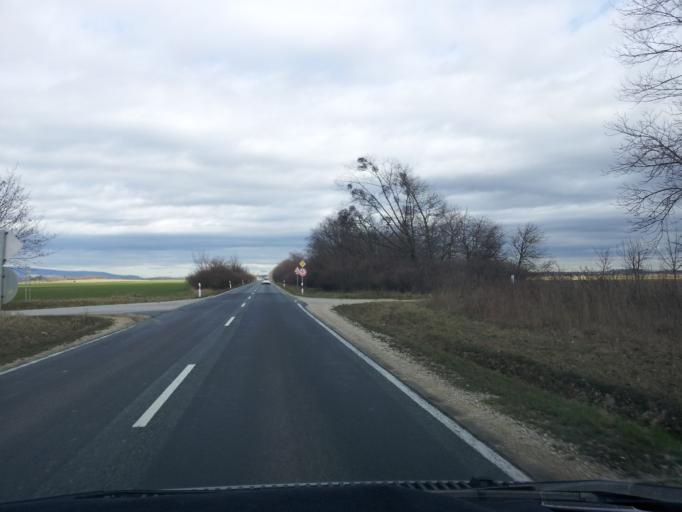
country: HU
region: Vas
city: Gencsapati
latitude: 47.2892
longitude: 16.6100
